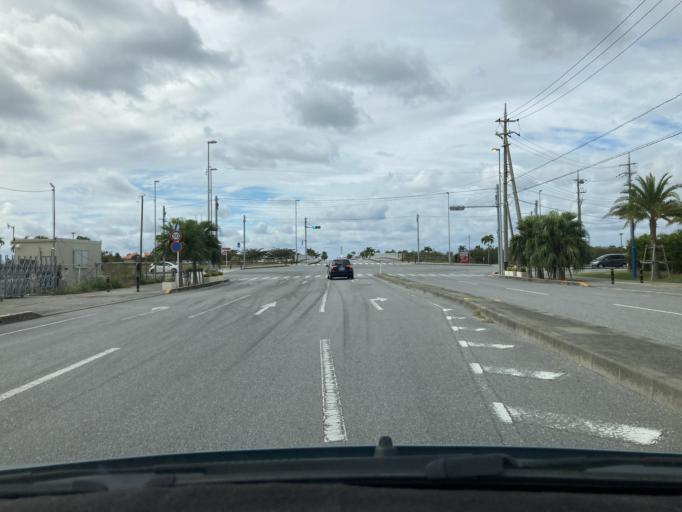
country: JP
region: Okinawa
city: Itoman
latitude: 26.1557
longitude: 127.6509
